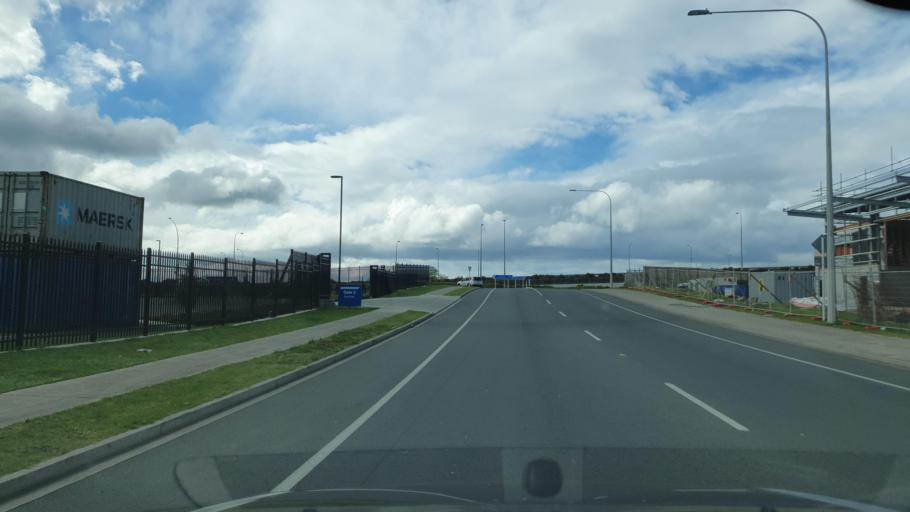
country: NZ
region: Bay of Plenty
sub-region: Tauranga City
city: Tauranga
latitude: -37.6918
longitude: 176.2406
